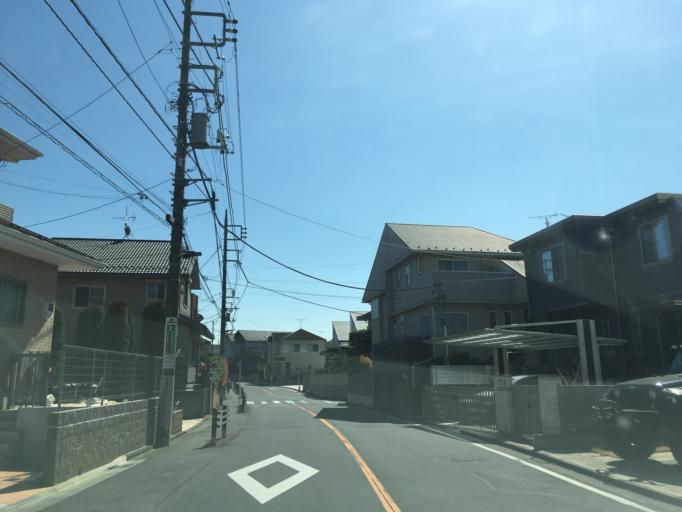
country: JP
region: Tokyo
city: Hino
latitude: 35.6430
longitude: 139.4440
